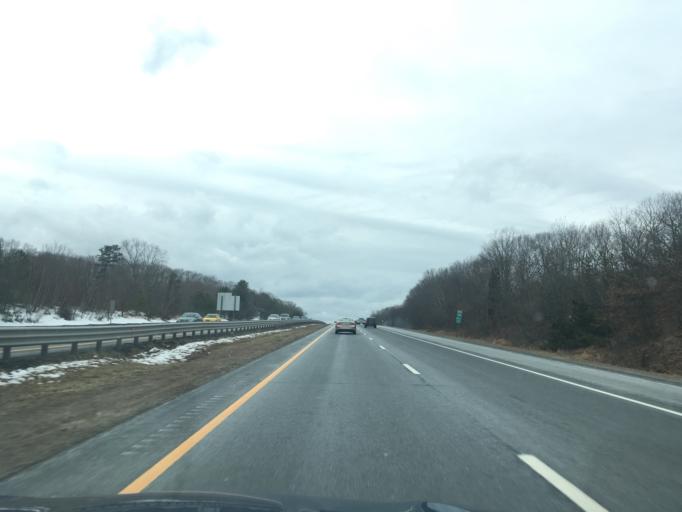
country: US
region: Rhode Island
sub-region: Kent County
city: West Warwick
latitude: 41.6646
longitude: -71.5179
